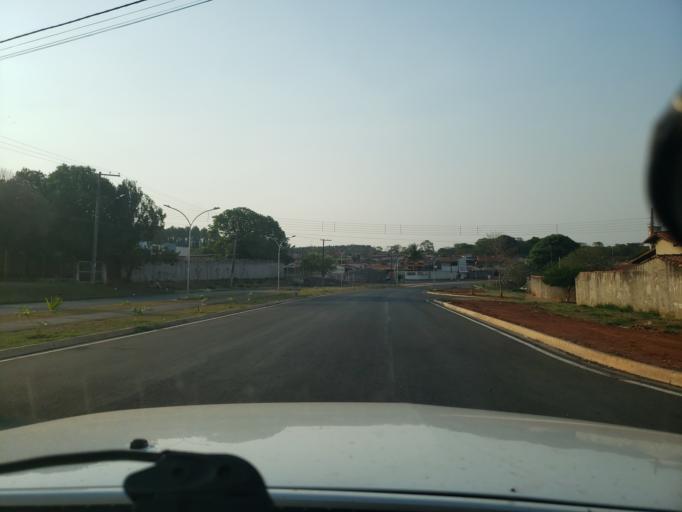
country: BR
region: Sao Paulo
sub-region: Moji-Guacu
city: Mogi-Gaucu
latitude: -22.3280
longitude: -46.9503
